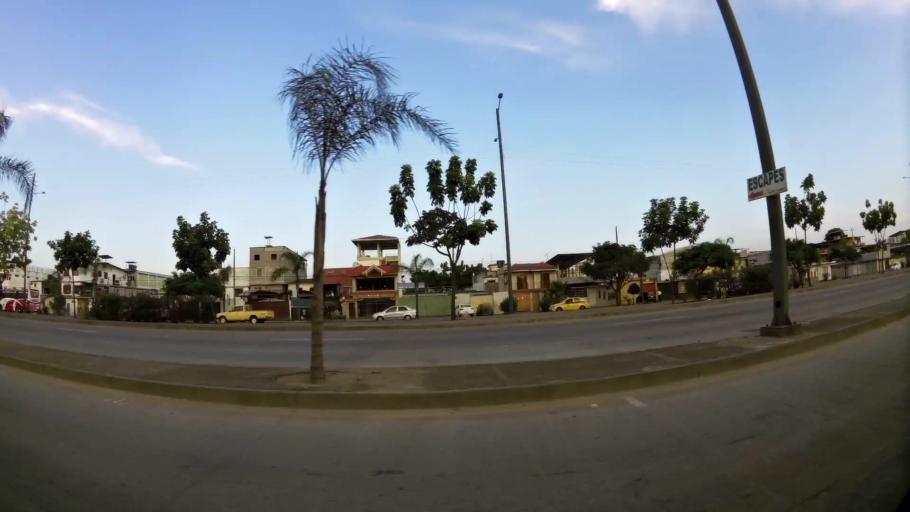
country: EC
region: Guayas
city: Eloy Alfaro
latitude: -2.1227
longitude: -79.8826
